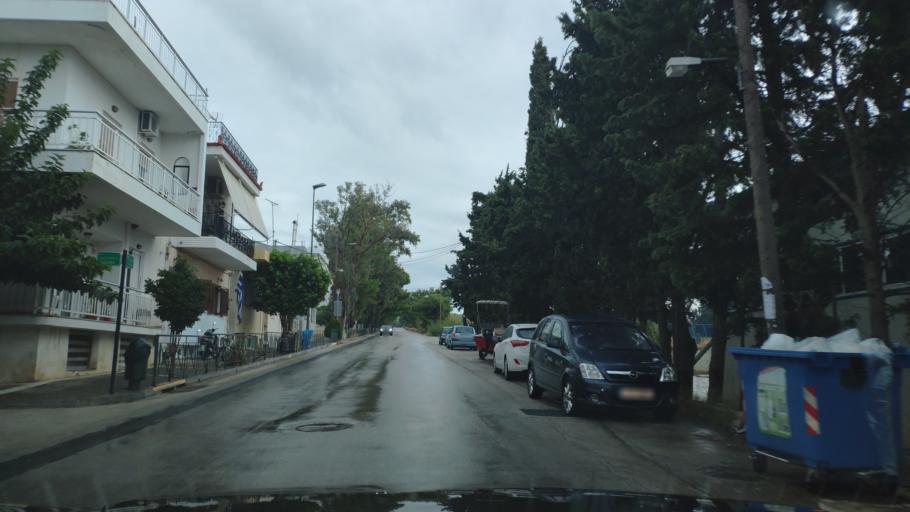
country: GR
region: Peloponnese
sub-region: Nomos Korinthias
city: Loutraki
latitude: 37.9673
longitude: 22.9820
